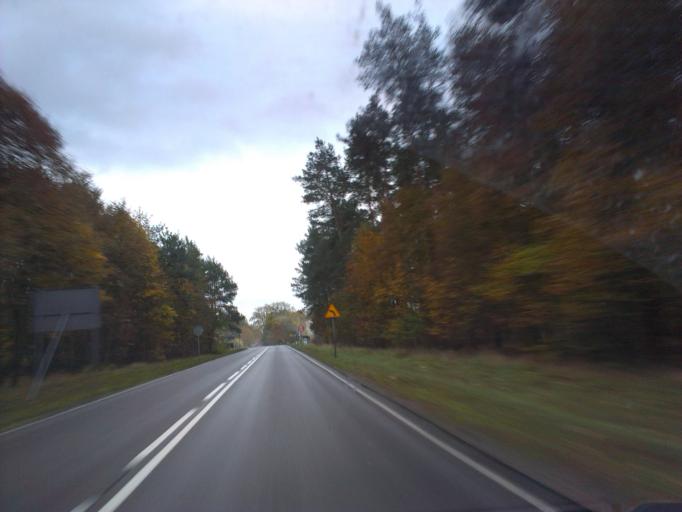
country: PL
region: Kujawsko-Pomorskie
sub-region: Powiat tucholski
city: Cekcyn
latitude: 53.5209
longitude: 17.9513
